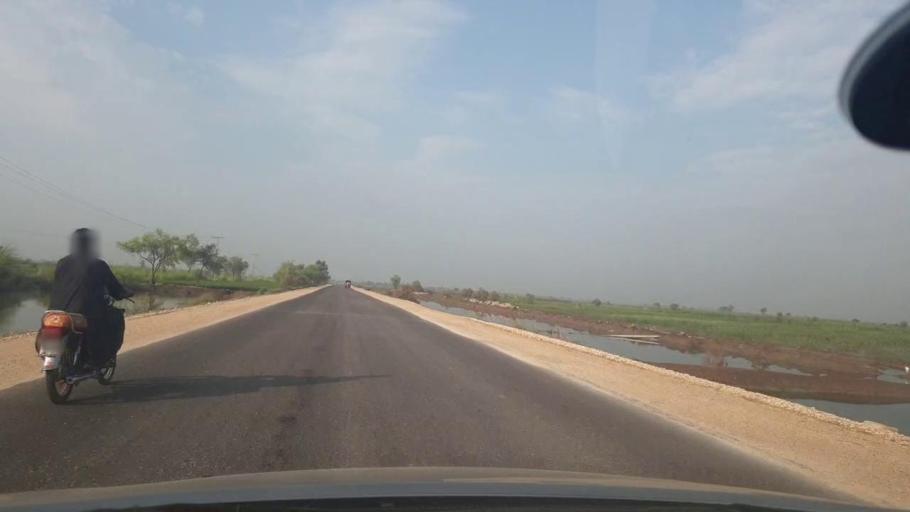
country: PK
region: Sindh
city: Jacobabad
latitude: 28.2286
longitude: 68.3816
